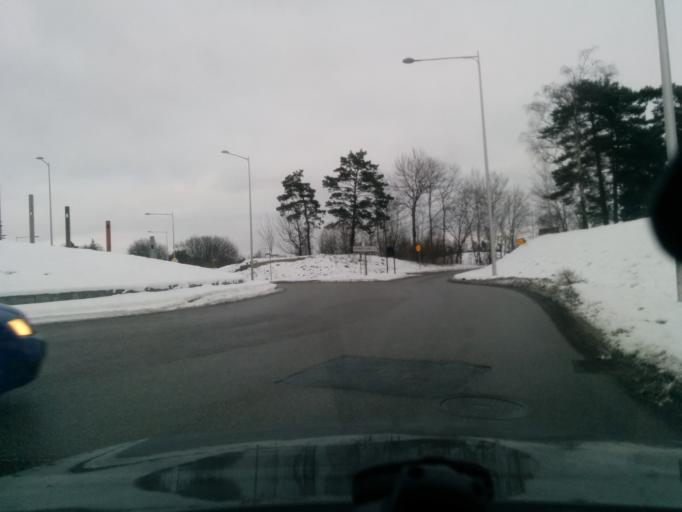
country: SE
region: Stockholm
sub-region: Taby Kommun
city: Taby
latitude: 59.4530
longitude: 18.0868
